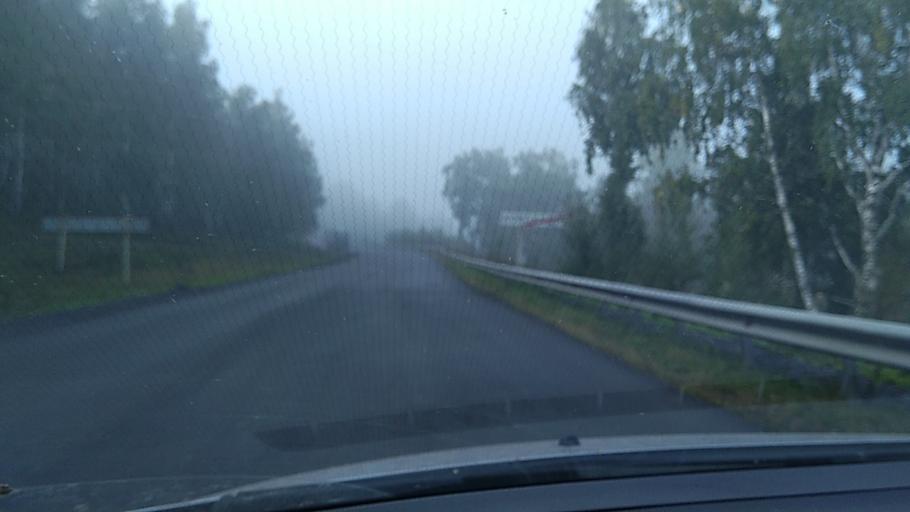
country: RU
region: Chelyabinsk
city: Karabash
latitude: 55.3394
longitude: 60.2423
